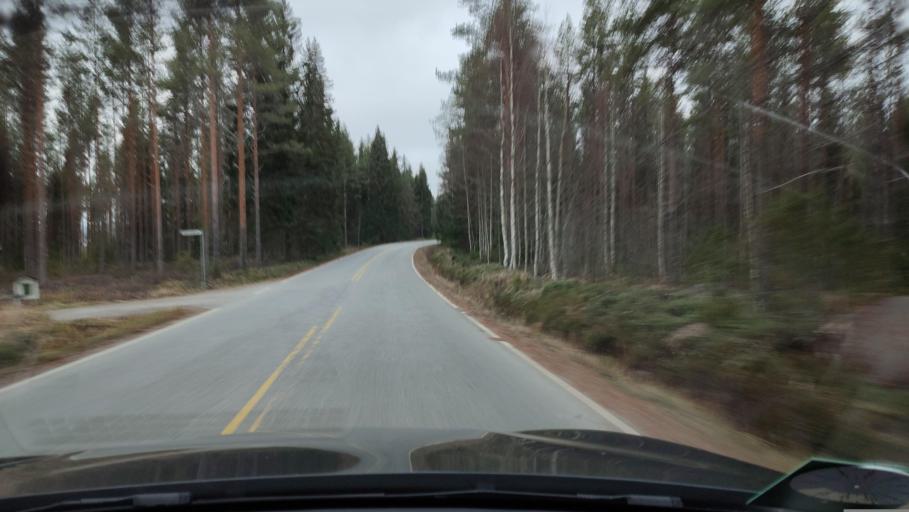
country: FI
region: Southern Ostrobothnia
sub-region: Suupohja
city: Karijoki
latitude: 62.2555
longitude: 21.7467
